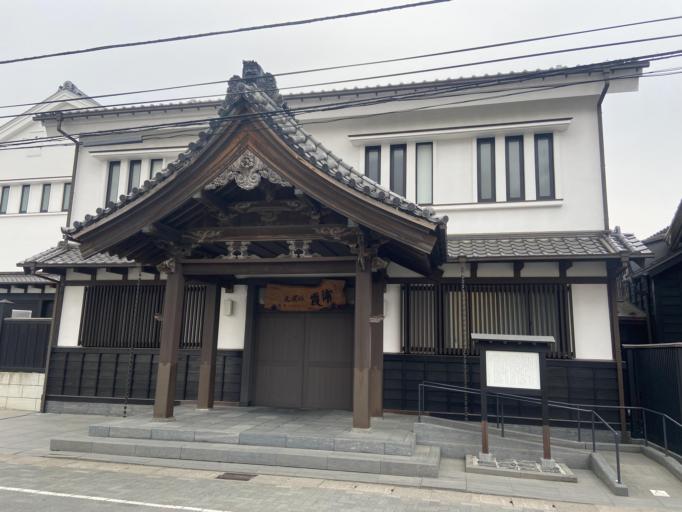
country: JP
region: Miyagi
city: Shiogama
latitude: 38.3164
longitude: 141.0190
